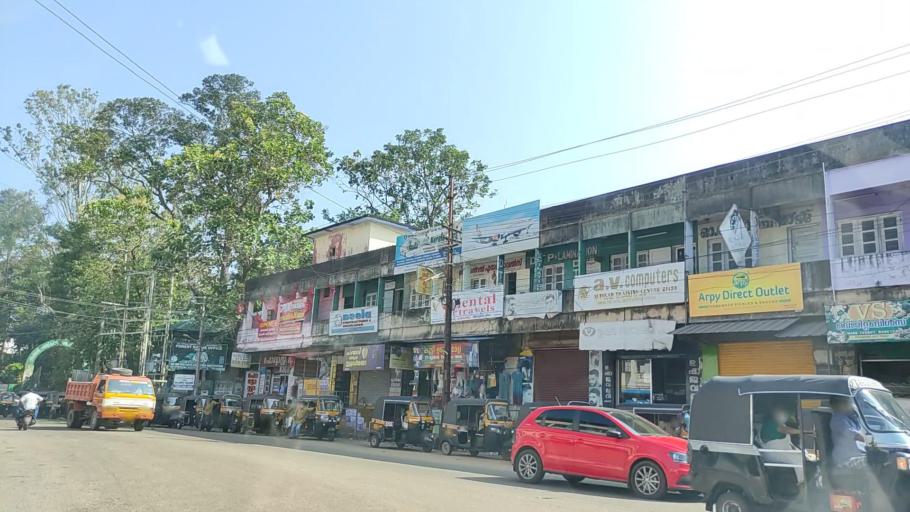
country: IN
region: Kerala
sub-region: Kollam
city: Punalur
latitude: 8.9275
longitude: 76.9140
